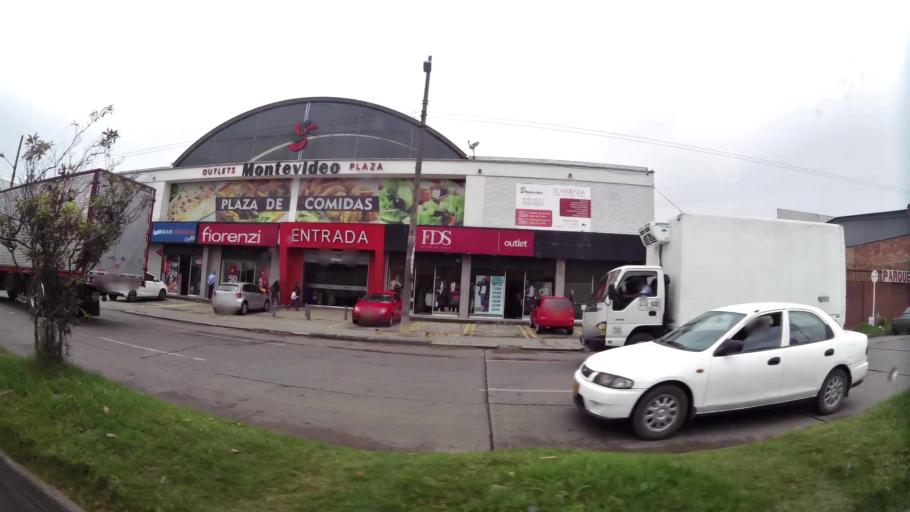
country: CO
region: Bogota D.C.
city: Bogota
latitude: 4.6482
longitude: -74.1199
